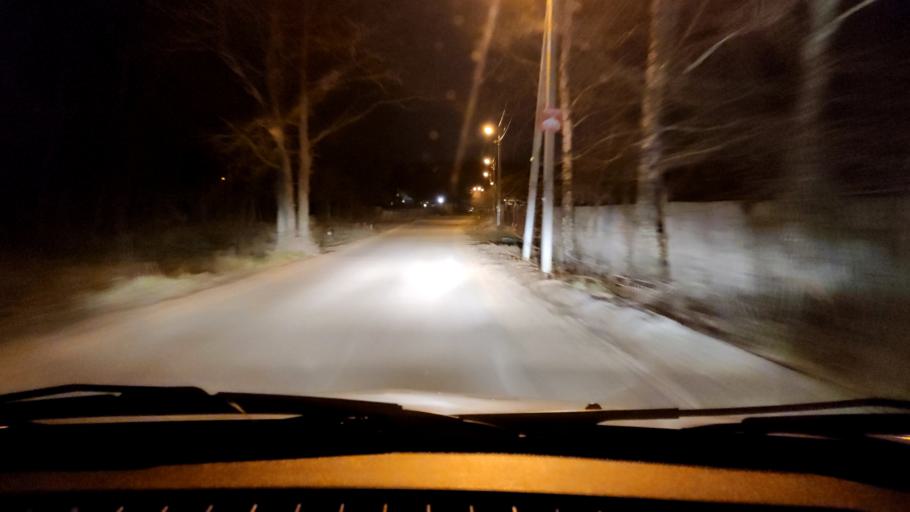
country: RU
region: Voronezj
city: Podgornoye
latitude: 51.7364
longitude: 39.1872
